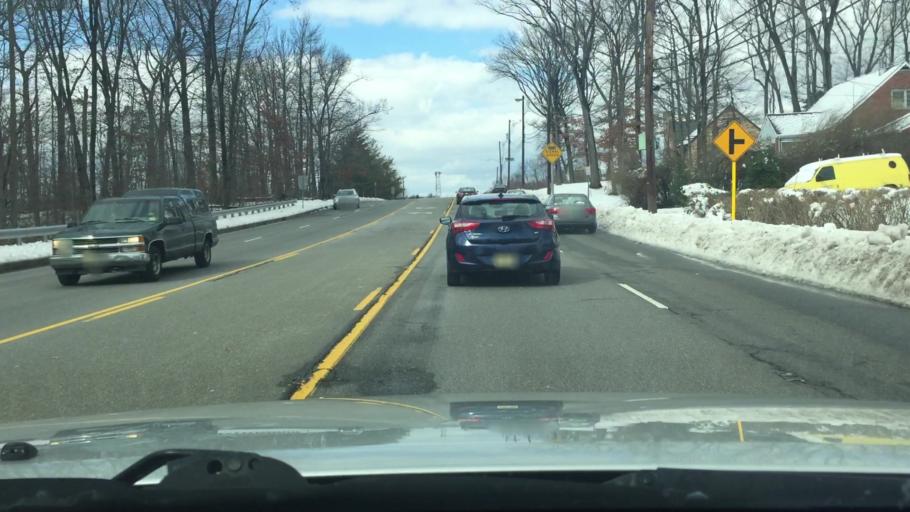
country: US
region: New Jersey
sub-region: Middlesex County
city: East Brunswick
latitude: 40.4396
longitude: -74.4230
